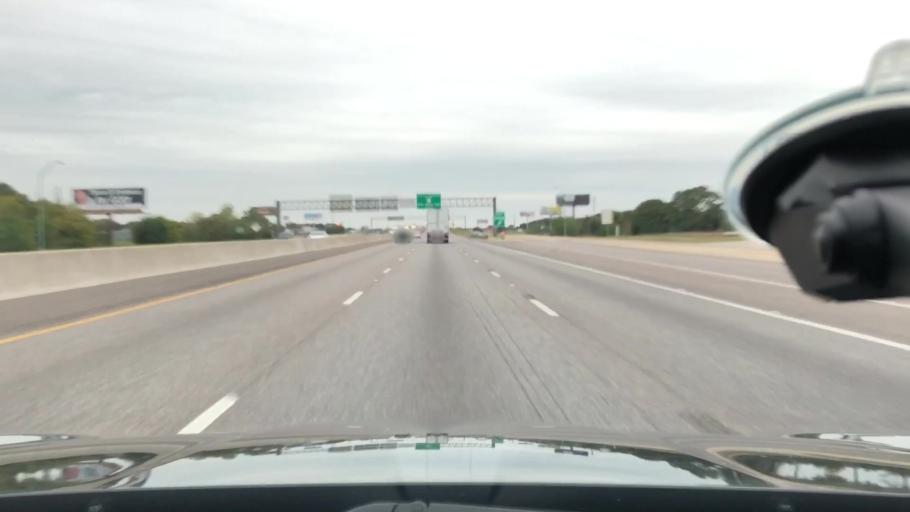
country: US
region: Texas
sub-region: McLennan County
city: Northcrest
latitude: 31.6331
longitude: -97.0957
